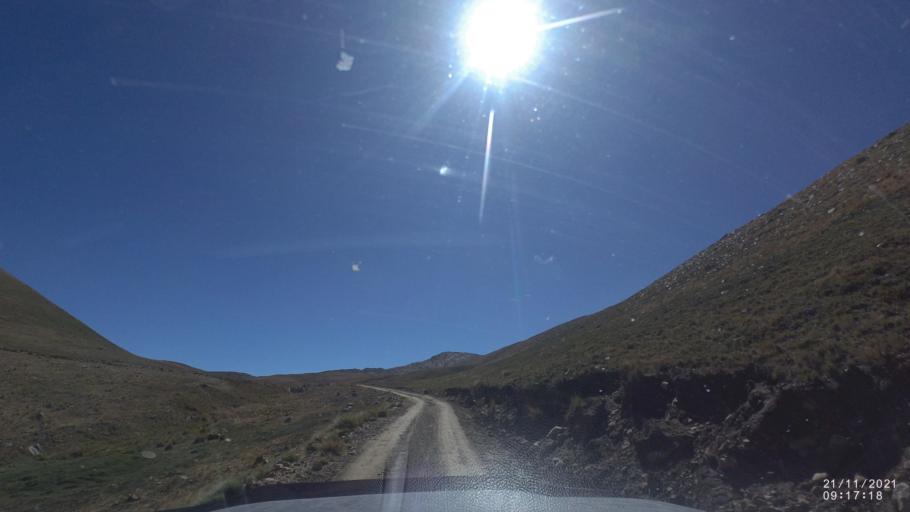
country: BO
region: Cochabamba
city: Cochabamba
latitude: -17.1227
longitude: -66.2573
